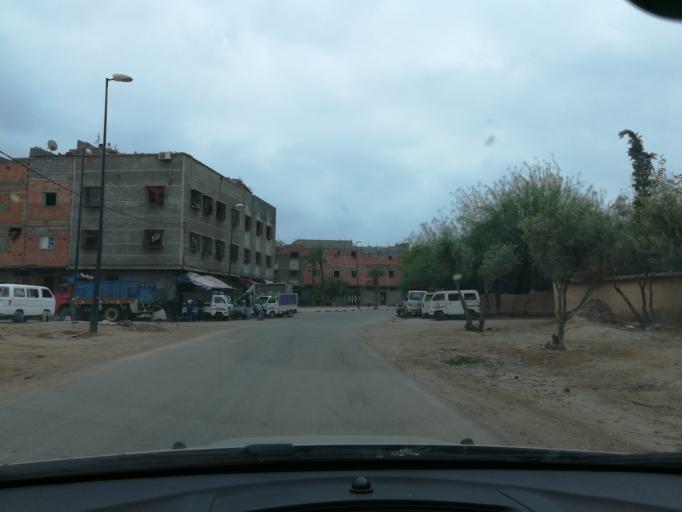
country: MA
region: Marrakech-Tensift-Al Haouz
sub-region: Marrakech
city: Marrakesh
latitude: 31.6659
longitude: -7.9849
